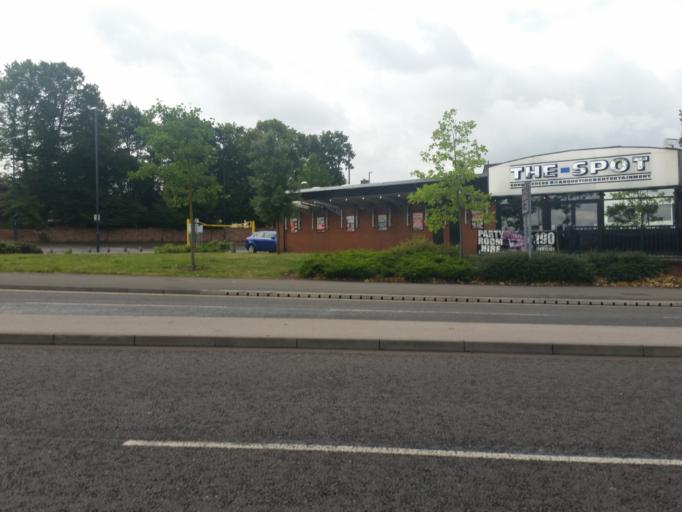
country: GB
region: England
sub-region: Derby
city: Derby
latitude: 52.9172
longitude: -1.4767
